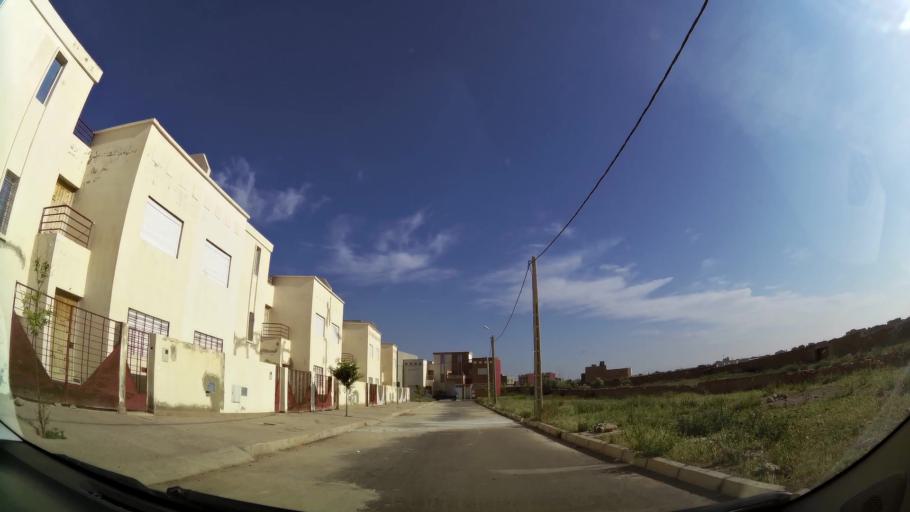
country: MA
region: Oriental
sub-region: Oujda-Angad
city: Oujda
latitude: 34.7229
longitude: -1.8879
